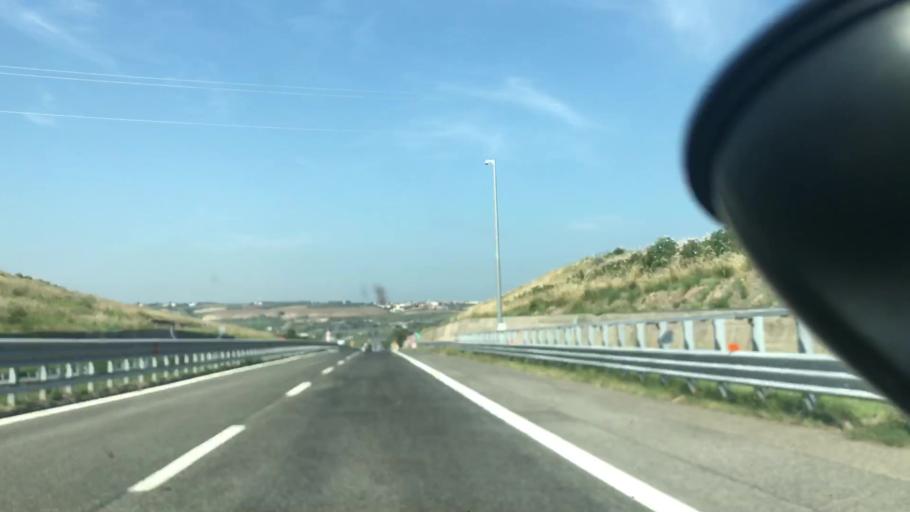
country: IT
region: Molise
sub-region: Provincia di Campobasso
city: Campomarino
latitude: 41.9490
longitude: 15.0236
